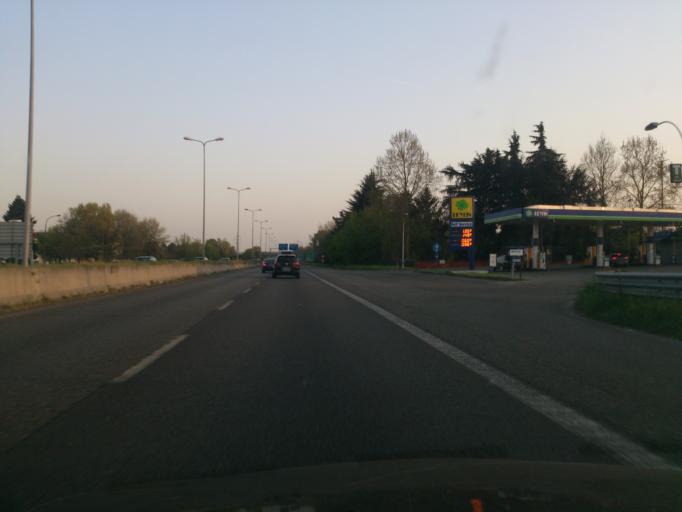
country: IT
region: Lombardy
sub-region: Citta metropolitana di Milano
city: Paderno Dugnano
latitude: 45.5748
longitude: 9.1761
